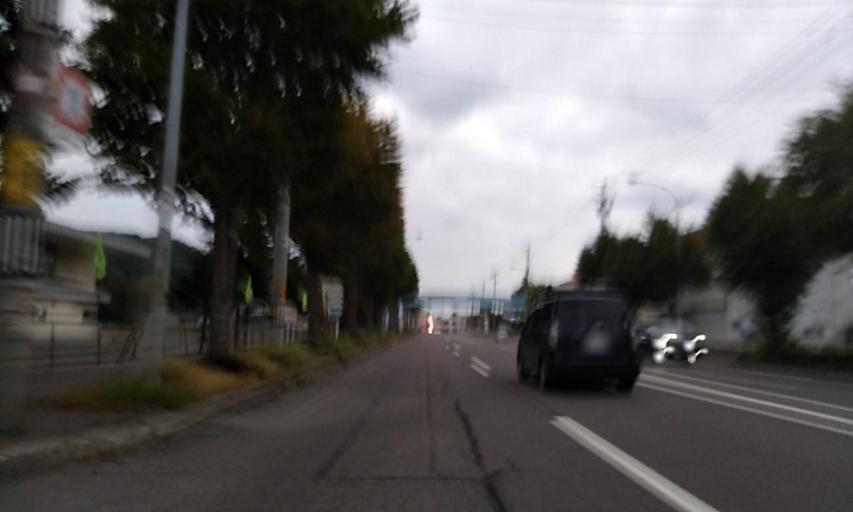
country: JP
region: Hokkaido
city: Abashiri
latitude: 44.0188
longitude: 144.2455
